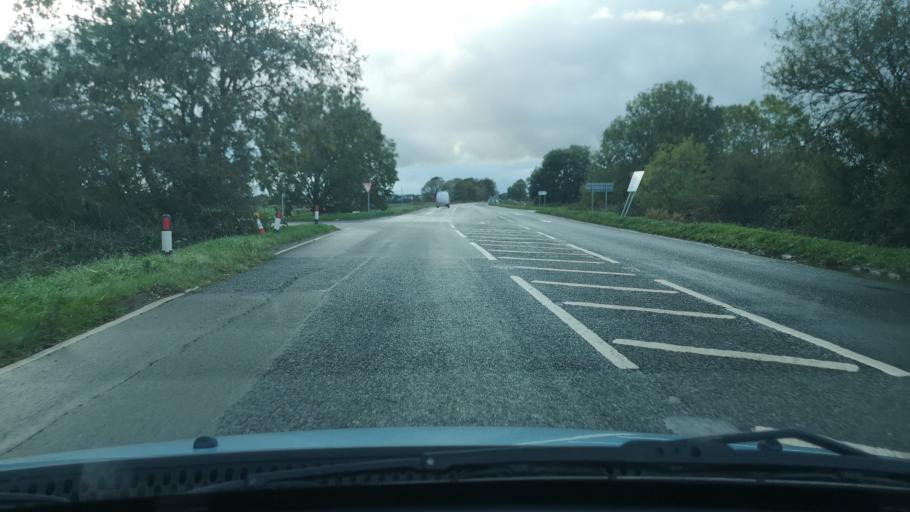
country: GB
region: England
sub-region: North Lincolnshire
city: Crowle
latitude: 53.5802
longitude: -0.8822
